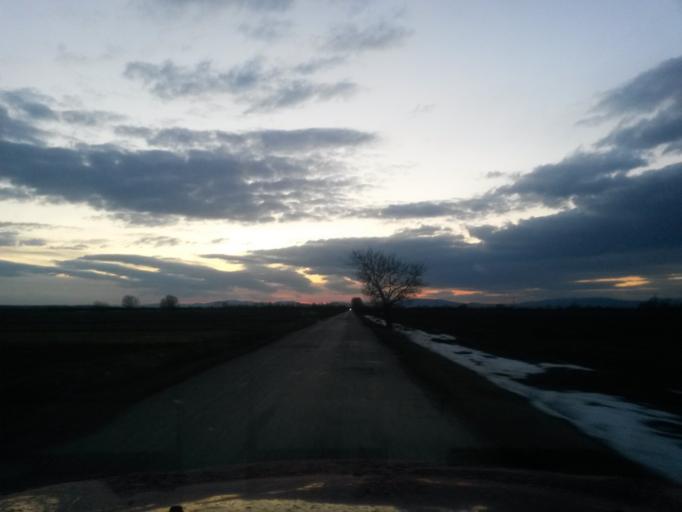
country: SK
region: Kosicky
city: Michalovce
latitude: 48.6978
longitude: 22.0168
